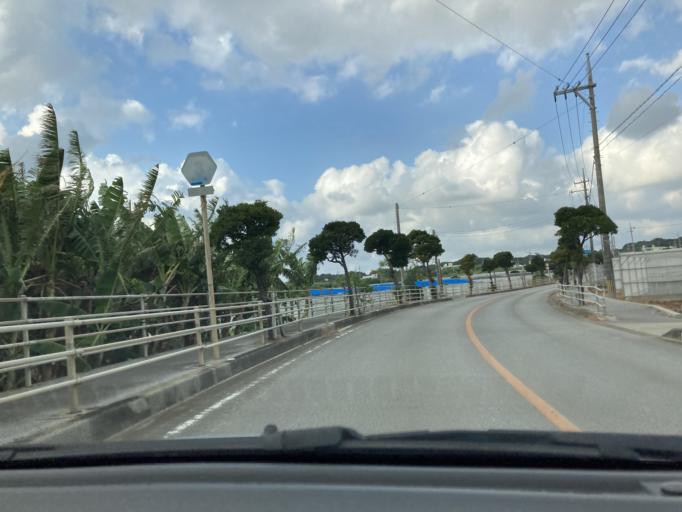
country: JP
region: Okinawa
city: Itoman
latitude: 26.1004
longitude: 127.6656
